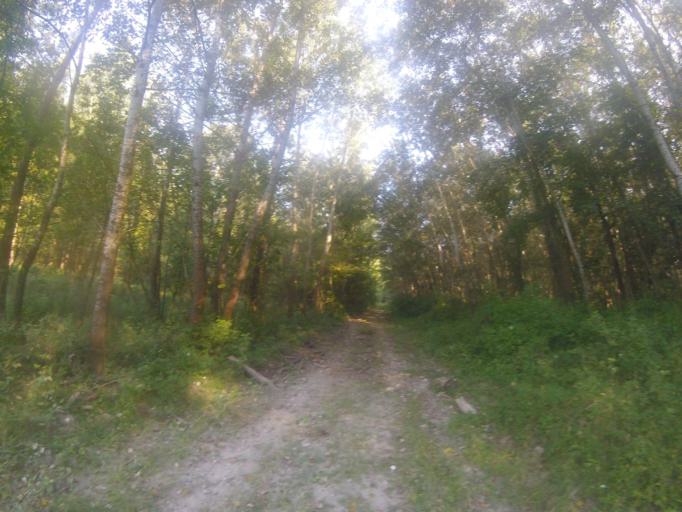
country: HU
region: Bacs-Kiskun
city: Baja
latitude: 46.1839
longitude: 18.9181
